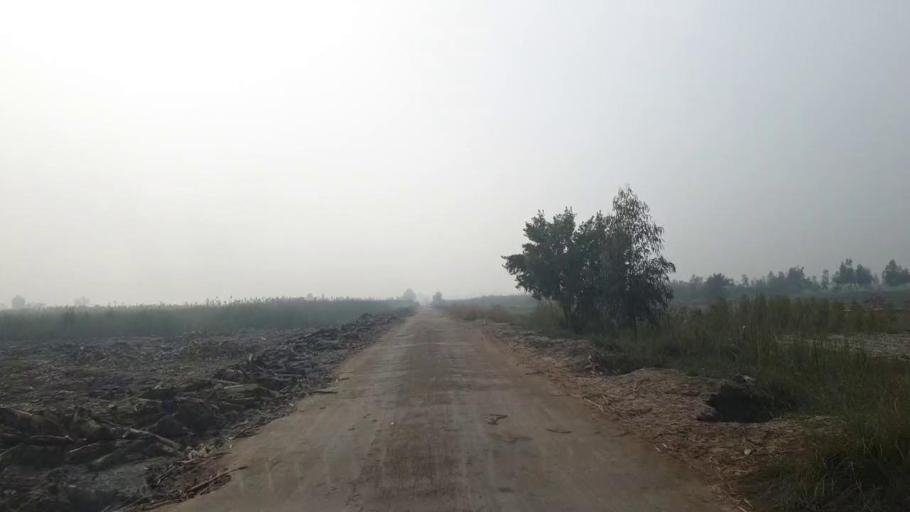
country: PK
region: Sindh
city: Tando Adam
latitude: 25.7794
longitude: 68.6073
